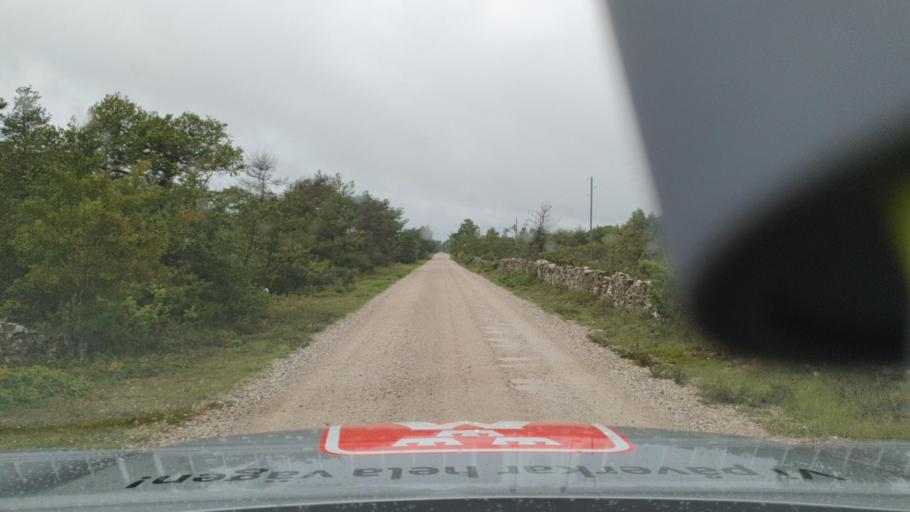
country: SE
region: Gotland
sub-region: Gotland
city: Hemse
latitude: 56.9455
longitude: 18.2261
